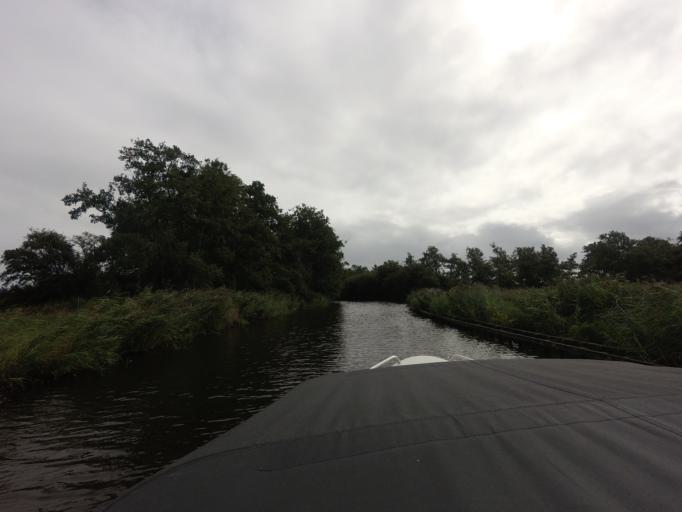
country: NL
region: Friesland
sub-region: Gemeente Boarnsterhim
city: Warten
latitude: 53.1270
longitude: 5.9044
